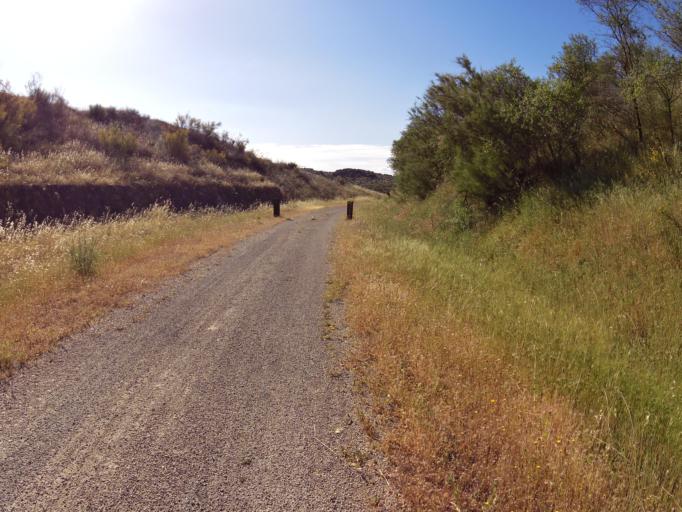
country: ES
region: Andalusia
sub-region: Province of Cordoba
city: Fuente-Tojar
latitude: 37.5824
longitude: -4.1866
